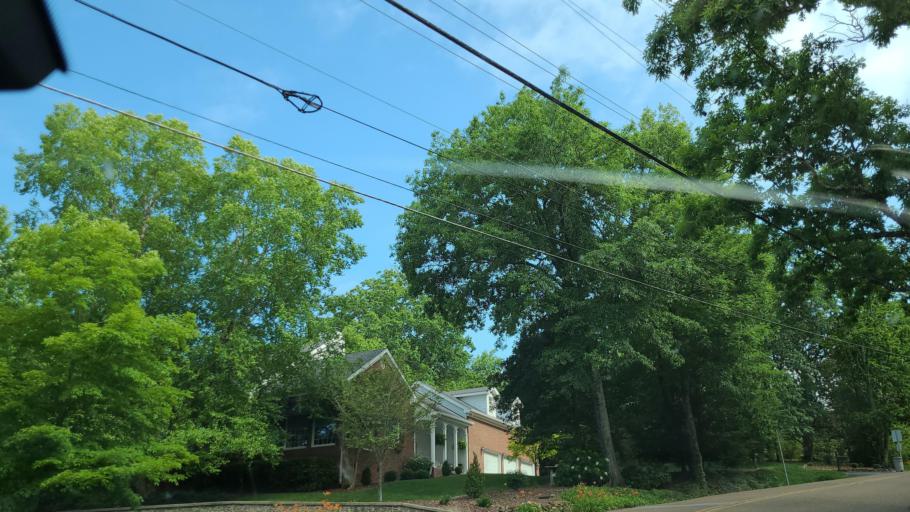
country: US
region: Tennessee
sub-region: Hamilton County
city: Lookout Mountain
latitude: 34.9963
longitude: -85.3484
